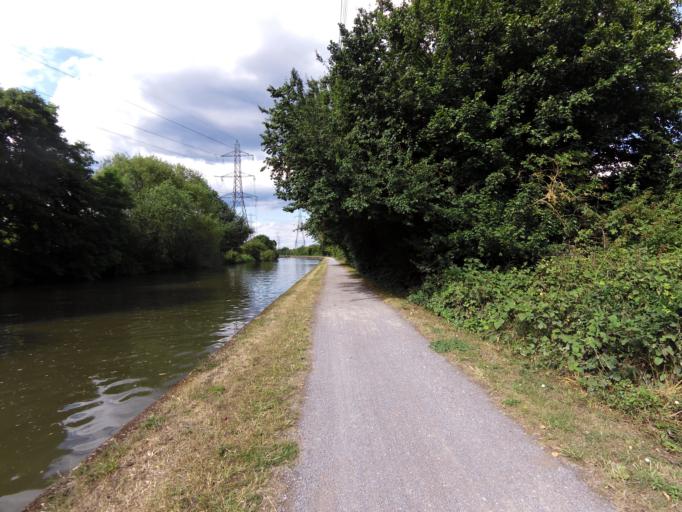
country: GB
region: England
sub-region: Greater London
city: Walthamstow
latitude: 51.6303
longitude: -0.0307
